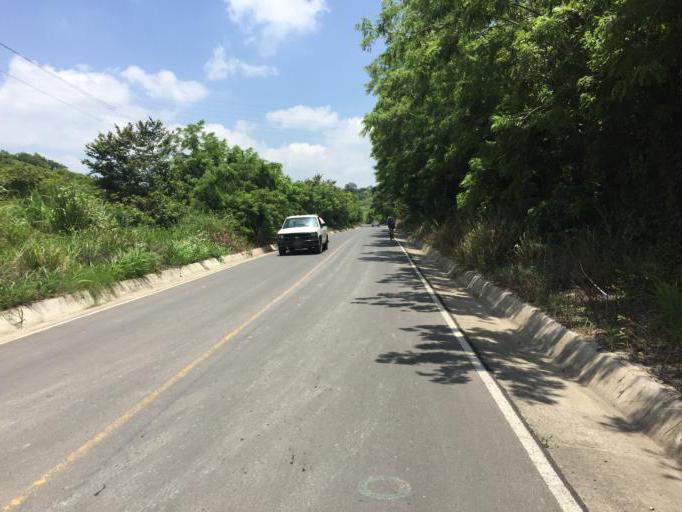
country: MX
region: Veracruz
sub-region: Tuxpan
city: Alto Lucero
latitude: 20.9396
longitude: -97.4367
